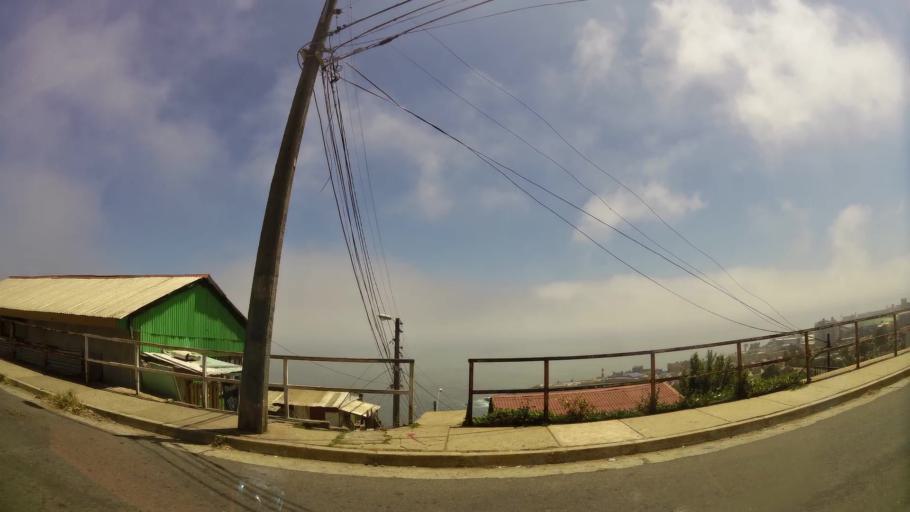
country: CL
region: Valparaiso
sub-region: Provincia de Valparaiso
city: Valparaiso
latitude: -33.0285
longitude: -71.6492
